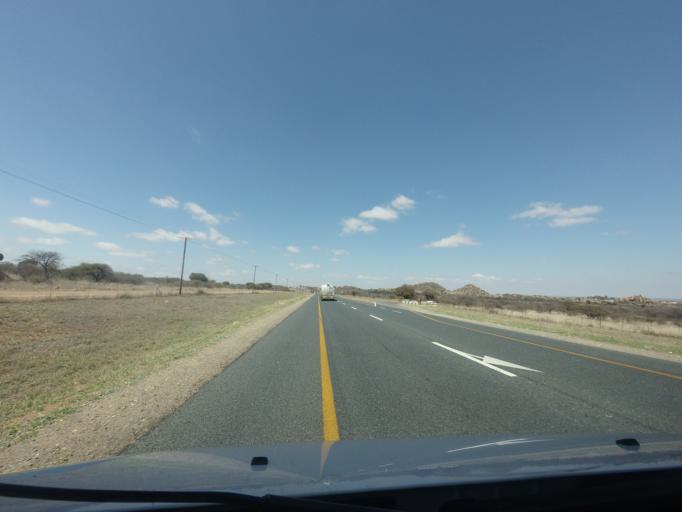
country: ZA
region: Limpopo
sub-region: Vhembe District Municipality
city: Louis Trichardt
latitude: -23.4267
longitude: 29.7493
